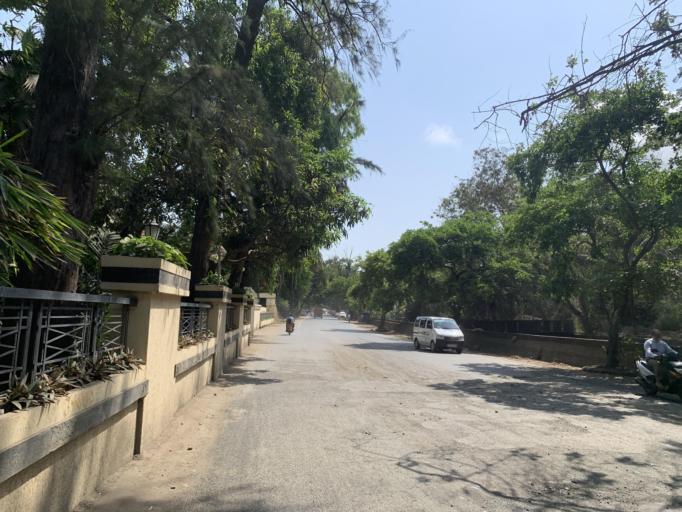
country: IN
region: Daman and Diu
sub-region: Daman District
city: Daman
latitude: 20.4504
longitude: 72.8366
